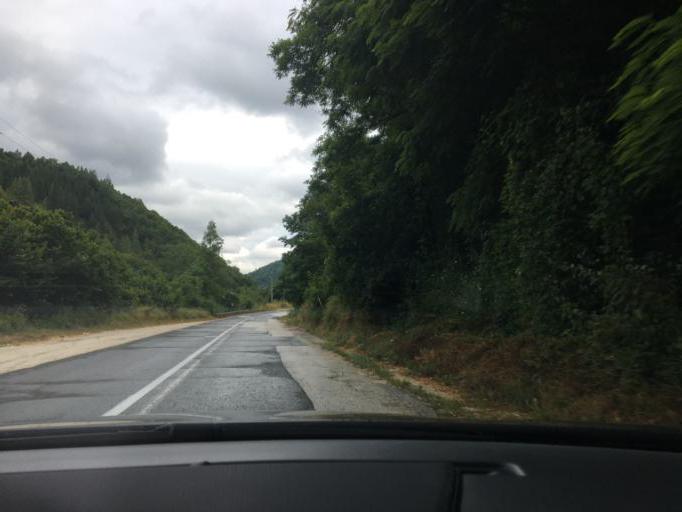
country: MK
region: Kriva Palanka
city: Kriva Palanka
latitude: 42.2246
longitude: 22.4162
